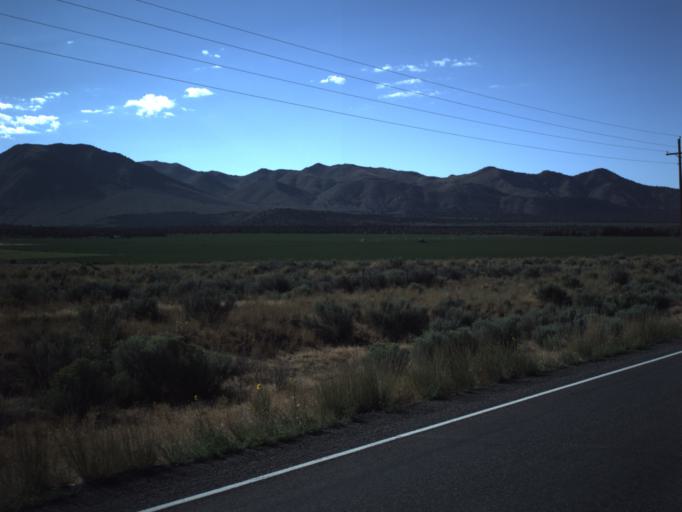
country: US
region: Utah
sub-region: Juab County
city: Mona
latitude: 39.8920
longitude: -112.1380
